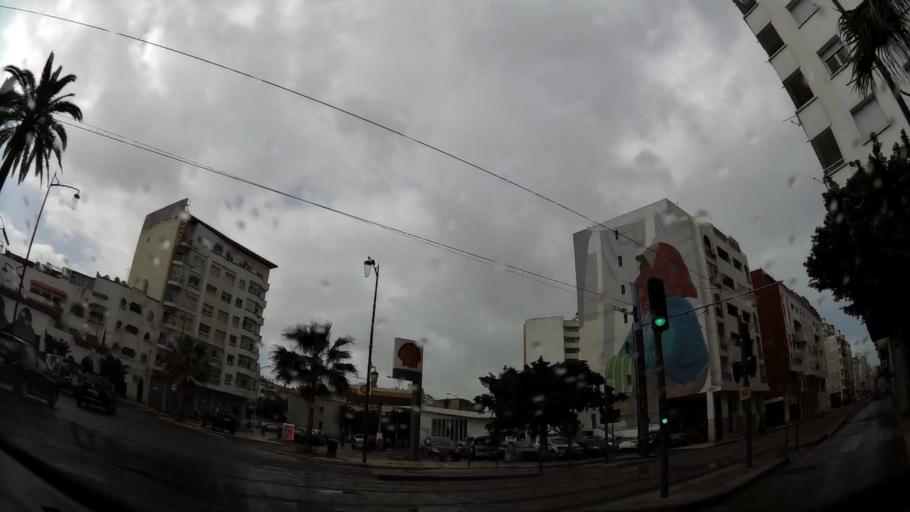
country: MA
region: Grand Casablanca
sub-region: Casablanca
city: Casablanca
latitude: 33.5934
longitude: -7.5983
